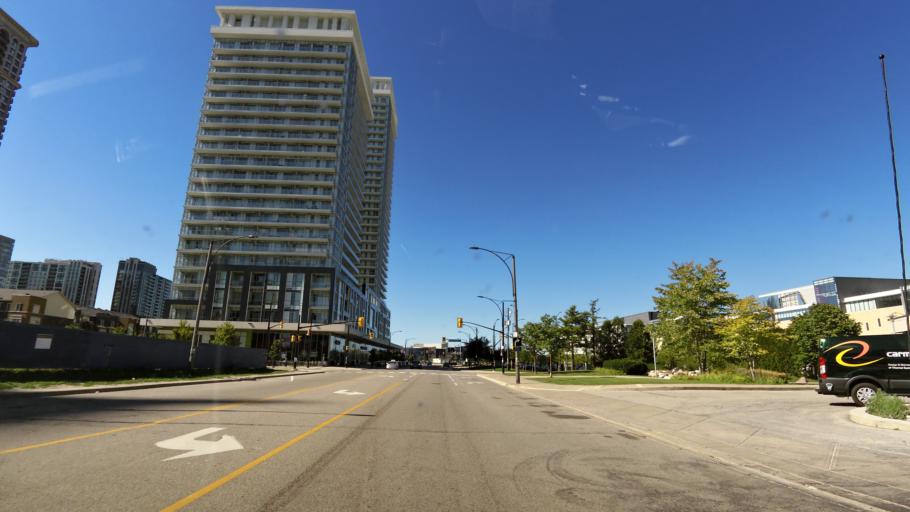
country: CA
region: Ontario
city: Mississauga
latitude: 43.5893
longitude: -79.6468
